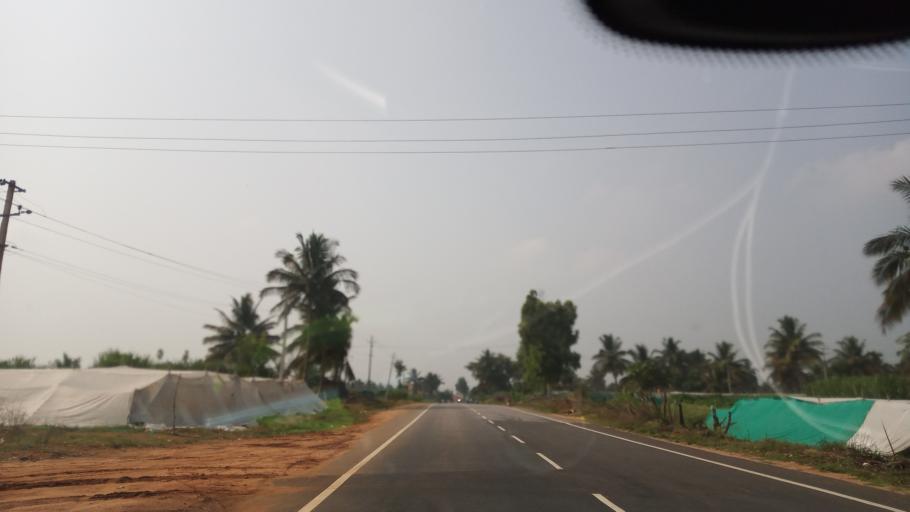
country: IN
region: Karnataka
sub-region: Mandya
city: Pandavapura
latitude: 12.5573
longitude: 76.6710
